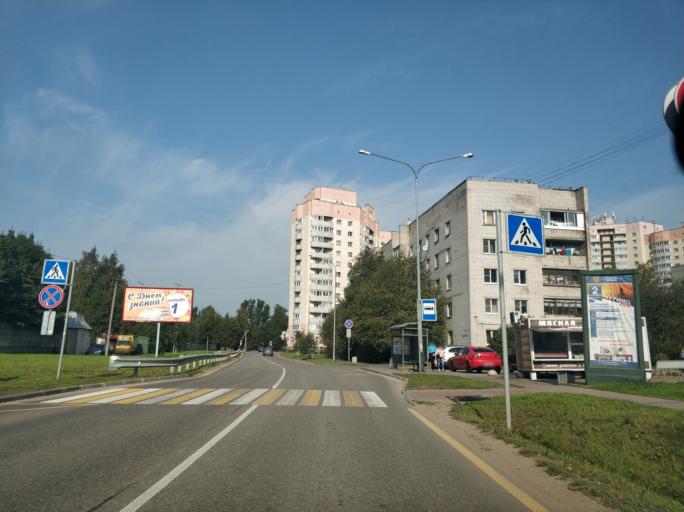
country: RU
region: Leningrad
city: Murino
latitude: 60.0451
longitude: 30.4629
